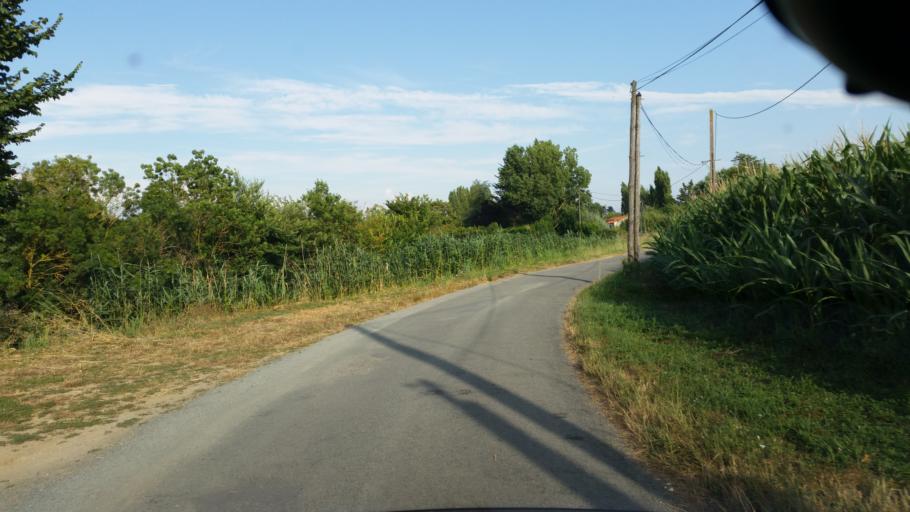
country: FR
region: Poitou-Charentes
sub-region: Departement de la Charente-Maritime
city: Marans
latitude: 46.3207
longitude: -0.9564
